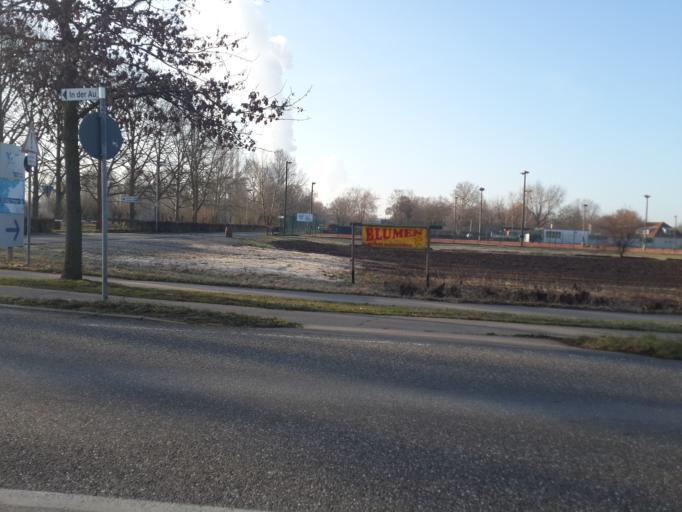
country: DE
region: Baden-Wuerttemberg
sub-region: Regierungsbezirk Stuttgart
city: Neckarsulm
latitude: 49.1930
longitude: 9.2073
